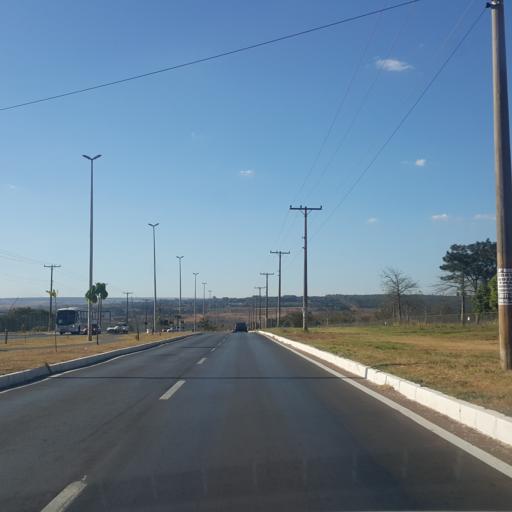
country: BR
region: Federal District
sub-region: Brasilia
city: Brasilia
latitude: -15.7904
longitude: -48.1179
